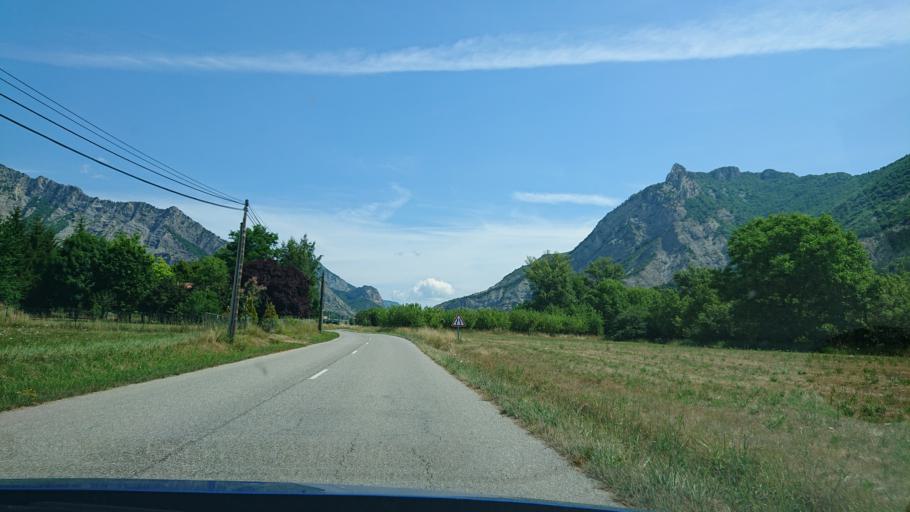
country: FR
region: Provence-Alpes-Cote d'Azur
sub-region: Departement des Hautes-Alpes
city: Tallard
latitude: 44.3484
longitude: 6.0373
